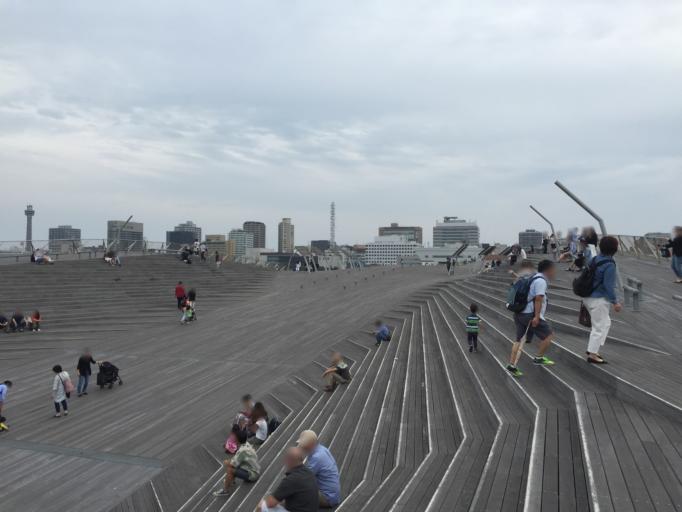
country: JP
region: Kanagawa
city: Yokohama
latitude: 35.4527
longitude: 139.6483
